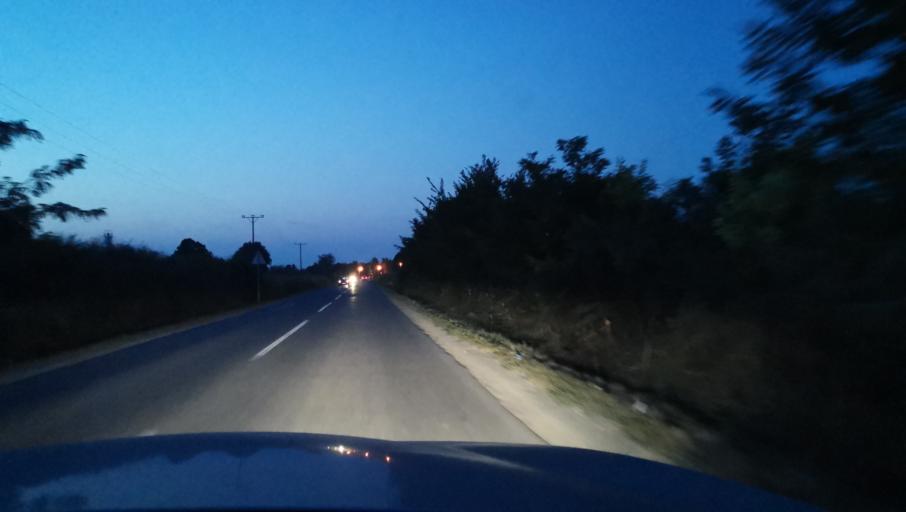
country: RS
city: Boljevci
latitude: 44.7404
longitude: 20.2525
